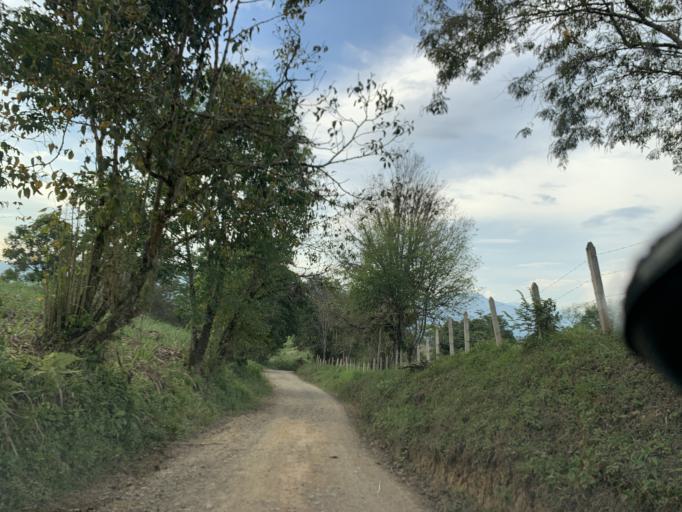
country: CO
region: Boyaca
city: Santana
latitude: 6.0706
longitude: -73.4851
